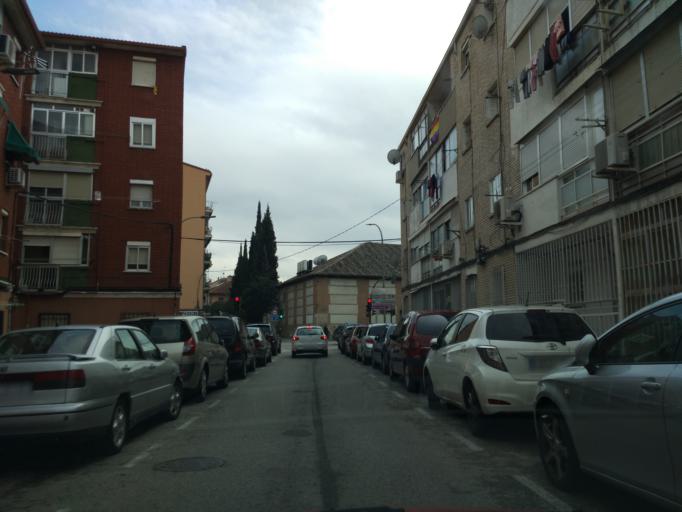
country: ES
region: Madrid
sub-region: Provincia de Madrid
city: Torrejon de Ardoz
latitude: 40.4623
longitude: -3.4826
